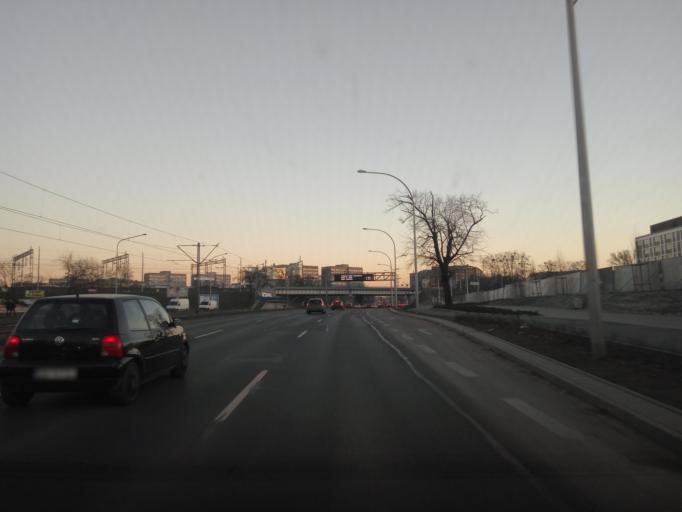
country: PL
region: Lower Silesian Voivodeship
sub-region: Powiat wroclawski
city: Wroclaw
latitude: 51.1196
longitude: 16.9968
